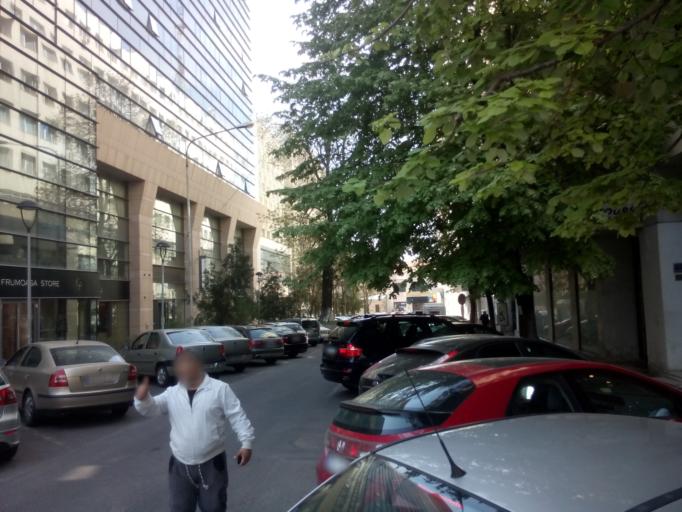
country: RO
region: Bucuresti
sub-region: Municipiul Bucuresti
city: Bucuresti
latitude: 44.4420
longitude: 26.0940
